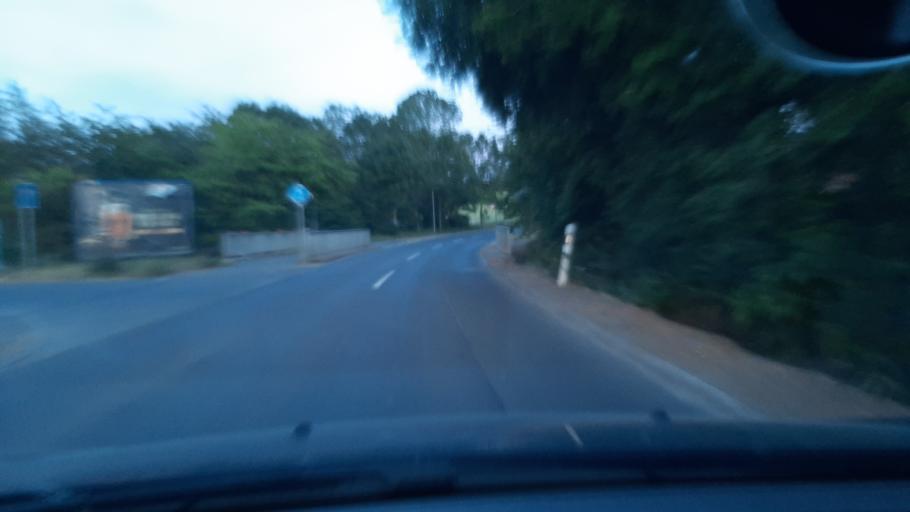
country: DE
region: North Rhine-Westphalia
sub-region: Regierungsbezirk Koln
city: Mechernich
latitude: 50.6164
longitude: 6.6574
